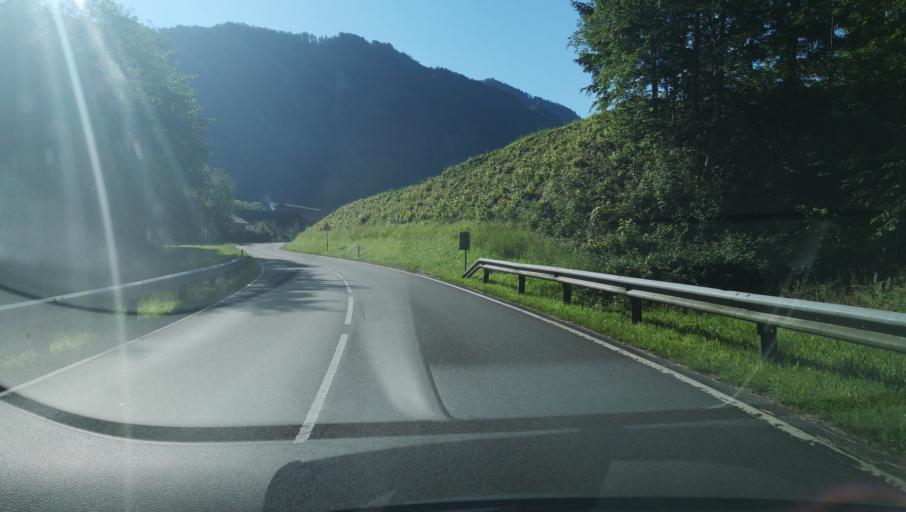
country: AT
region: Lower Austria
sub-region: Politischer Bezirk Amstetten
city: Ybbsitz
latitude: 47.9251
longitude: 14.8279
